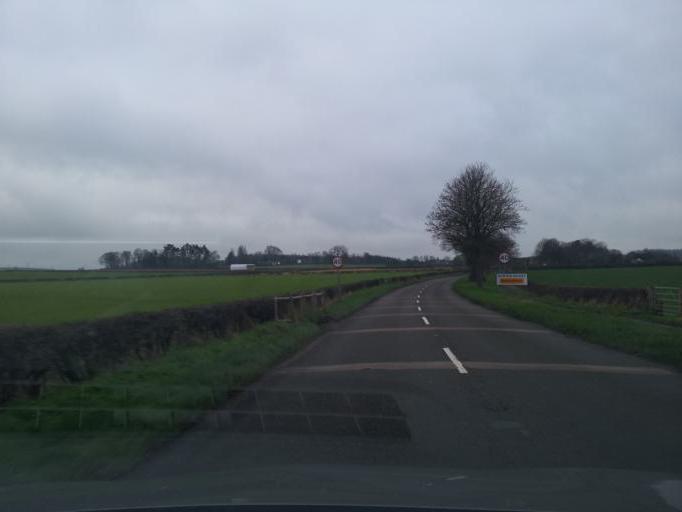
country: GB
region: England
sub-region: Derbyshire
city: Repton
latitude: 52.8311
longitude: -1.5727
